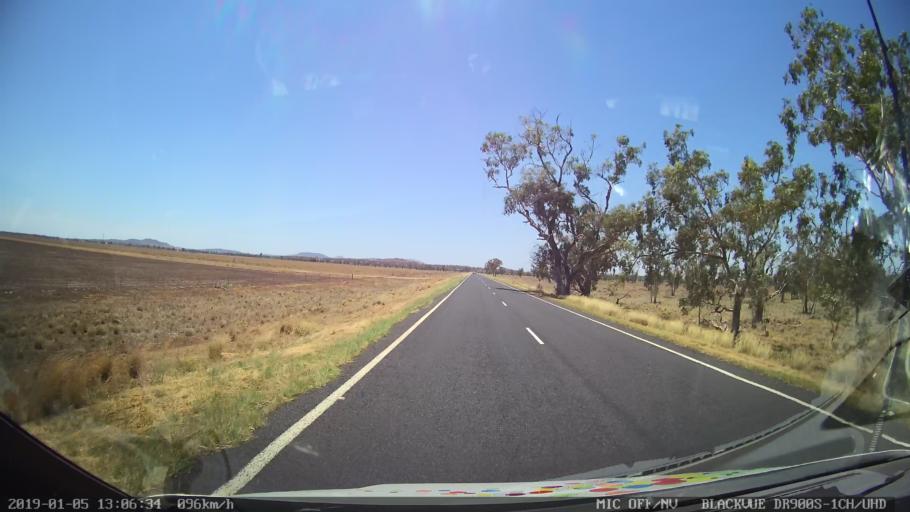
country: AU
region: New South Wales
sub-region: Gunnedah
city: Gunnedah
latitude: -31.0959
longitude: 149.8715
